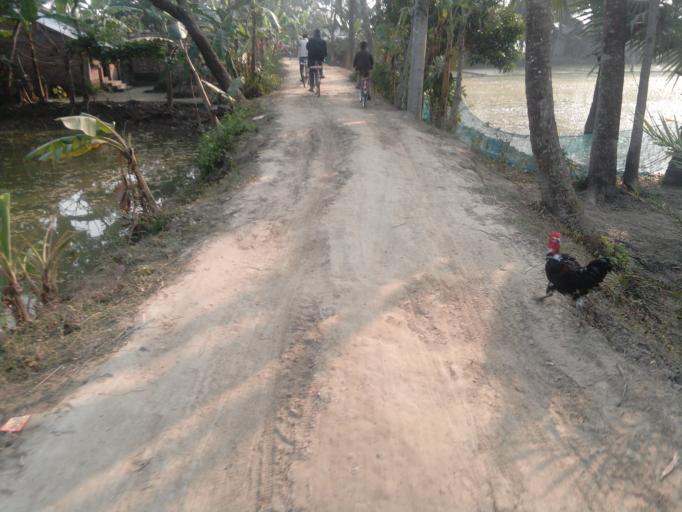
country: BD
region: Khulna
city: Kesabpur
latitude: 22.7672
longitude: 89.2285
